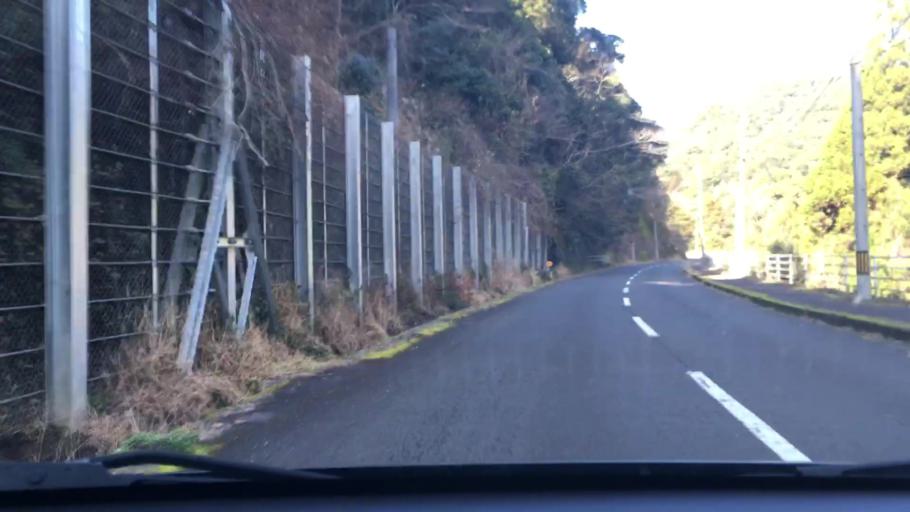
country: JP
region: Kagoshima
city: Satsumasendai
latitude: 31.7510
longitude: 130.4110
